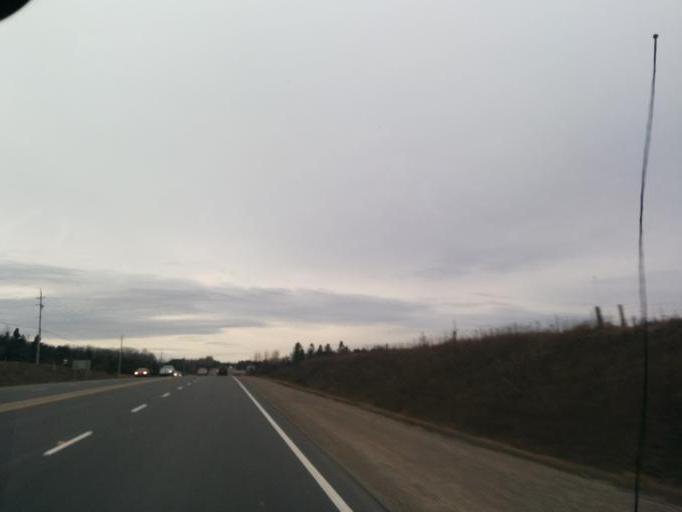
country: CA
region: Ontario
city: Shelburne
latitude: 44.0876
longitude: -80.1562
